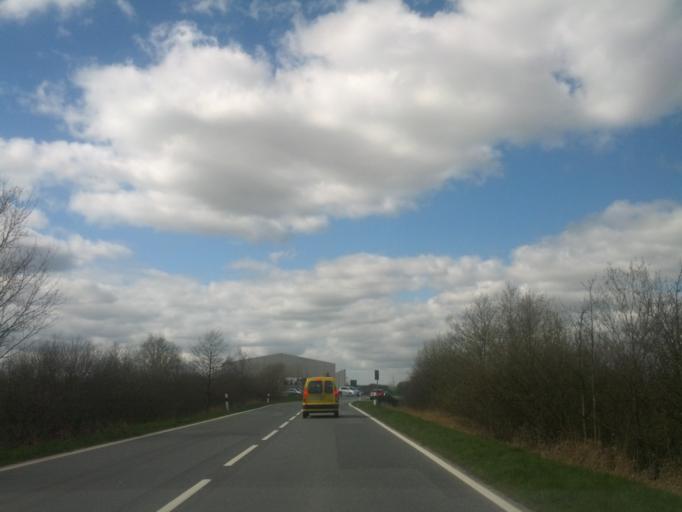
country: DE
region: Lower Saxony
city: Wittmund
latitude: 53.5853
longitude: 7.7850
